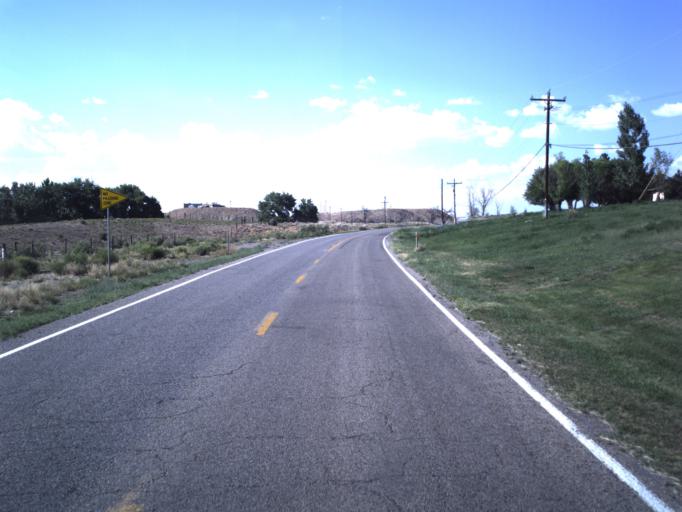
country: US
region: Utah
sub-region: Emery County
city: Huntington
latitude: 39.3615
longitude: -110.8521
